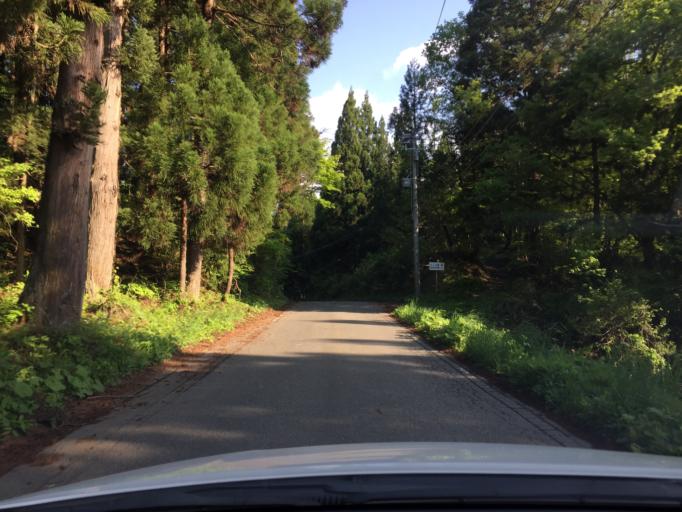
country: JP
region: Fukushima
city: Kitakata
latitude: 37.6743
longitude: 139.8058
